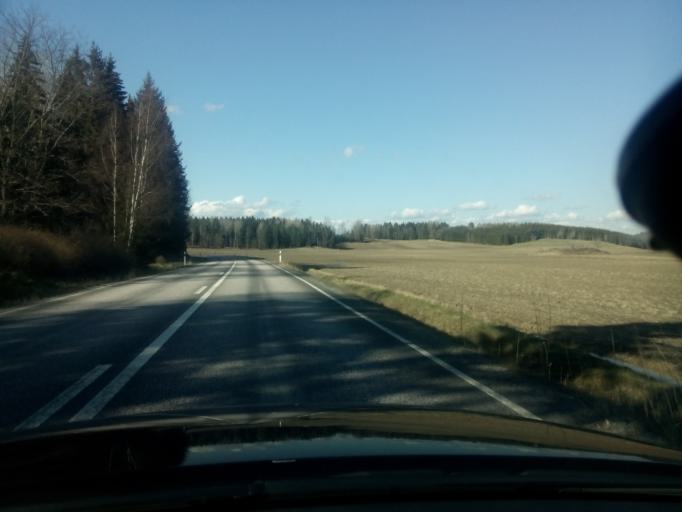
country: SE
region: Soedermanland
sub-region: Flens Kommun
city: Malmkoping
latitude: 59.0229
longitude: 16.8484
